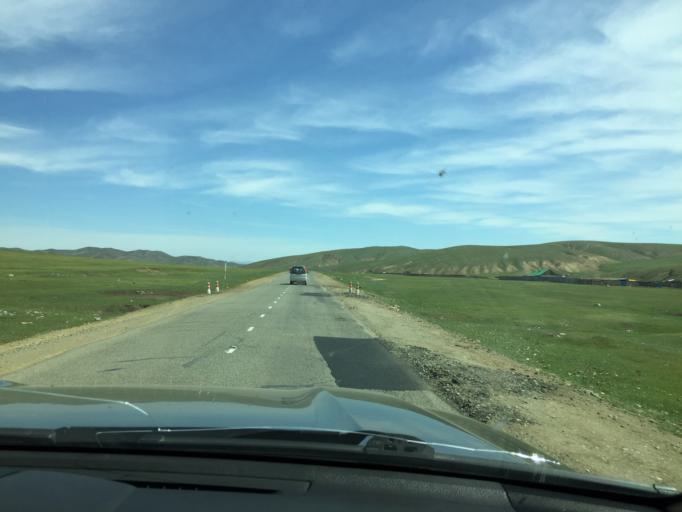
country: MN
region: Central Aimak
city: Bornuur
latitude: 48.6641
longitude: 106.1273
